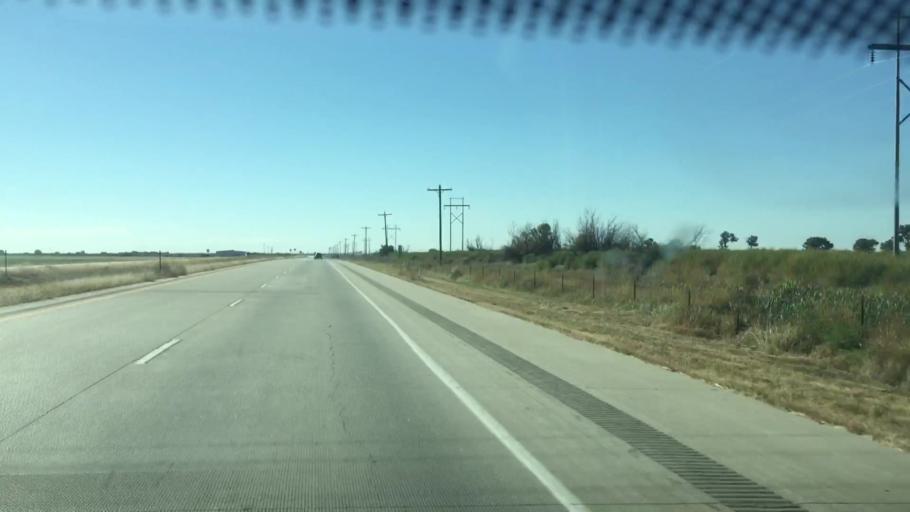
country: US
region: Colorado
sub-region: Prowers County
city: Lamar
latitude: 38.1098
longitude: -102.6819
